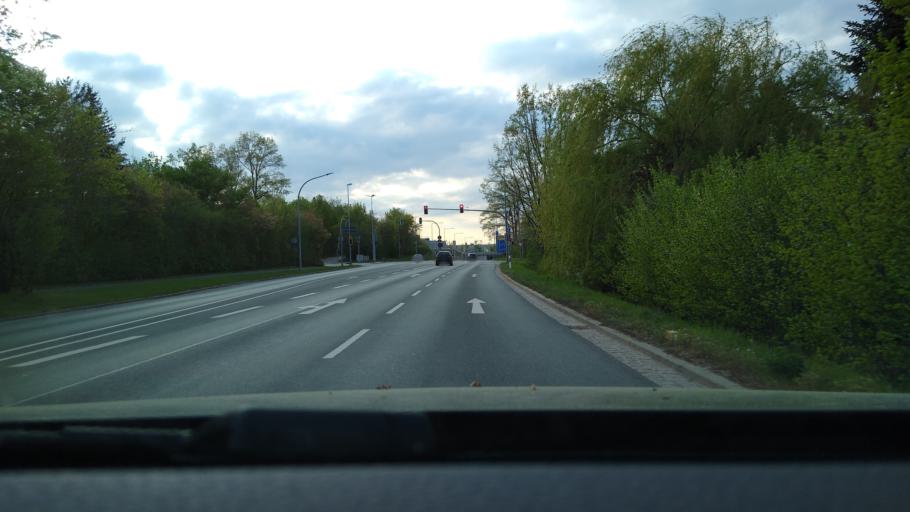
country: DE
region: Bavaria
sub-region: Regierungsbezirk Mittelfranken
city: Schwabach
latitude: 49.3186
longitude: 11.0488
